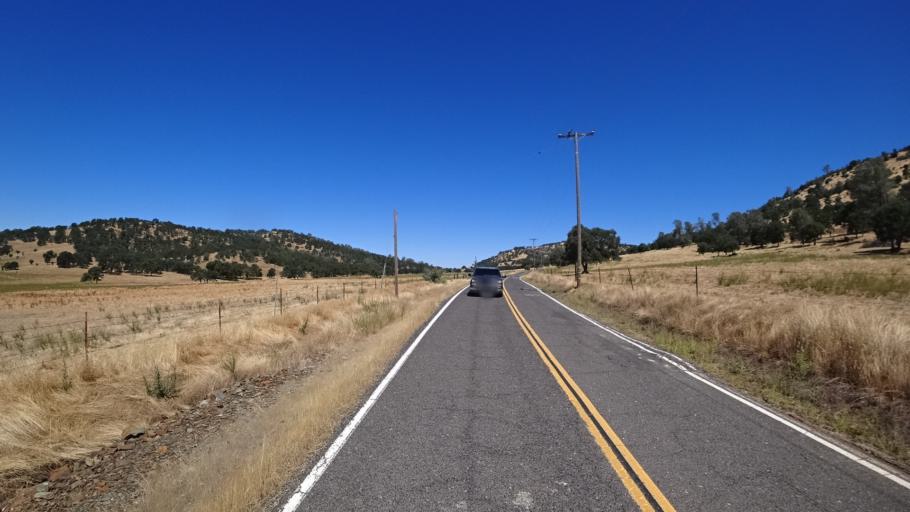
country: US
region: California
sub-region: Calaveras County
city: Copperopolis
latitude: 37.9895
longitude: -120.6502
